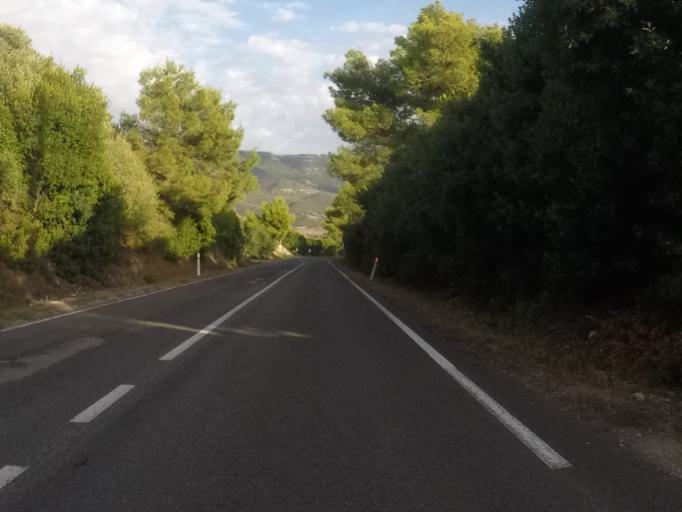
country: IT
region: Sardinia
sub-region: Provincia di Sassari
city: Alghero
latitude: 40.5123
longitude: 8.3540
